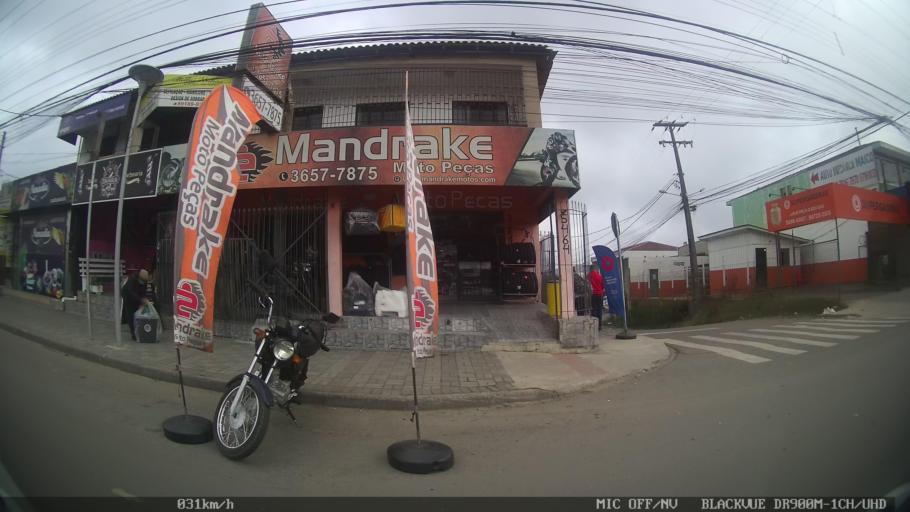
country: BR
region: Parana
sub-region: Almirante Tamandare
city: Almirante Tamandare
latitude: -25.3402
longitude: -49.2704
